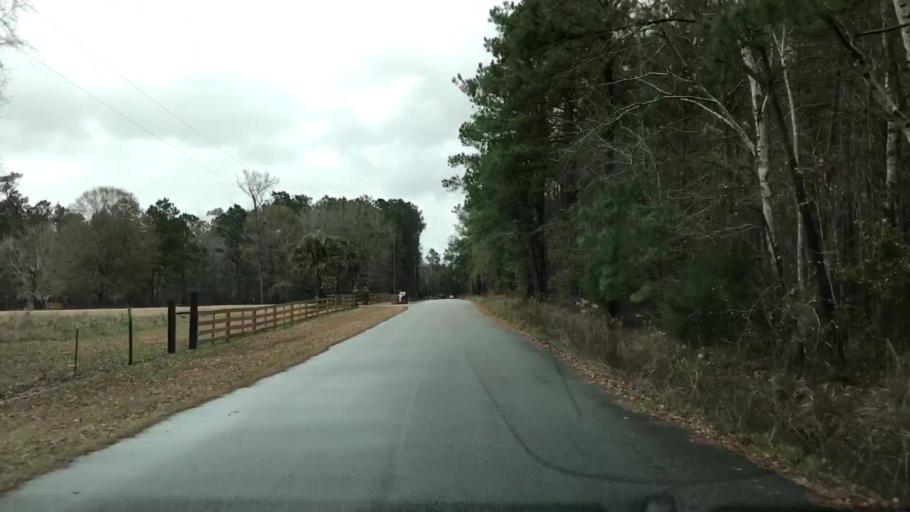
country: US
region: South Carolina
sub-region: Williamsburg County
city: Andrews
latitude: 33.4936
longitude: -79.5042
